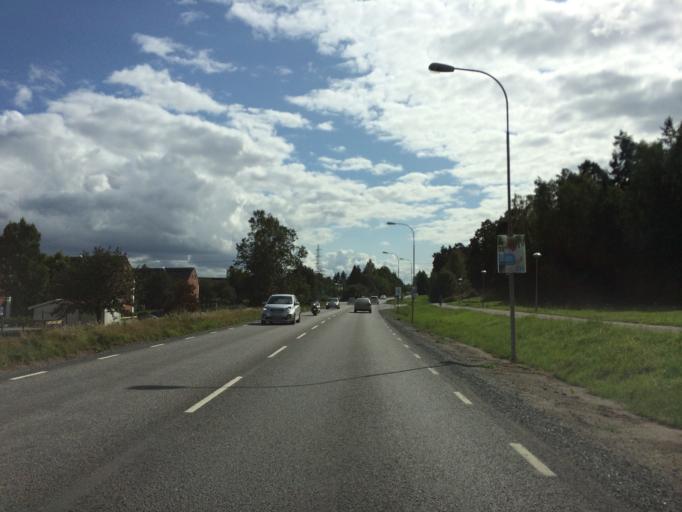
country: SE
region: Stockholm
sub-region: Sollentuna Kommun
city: Sollentuna
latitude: 59.4453
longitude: 17.9260
